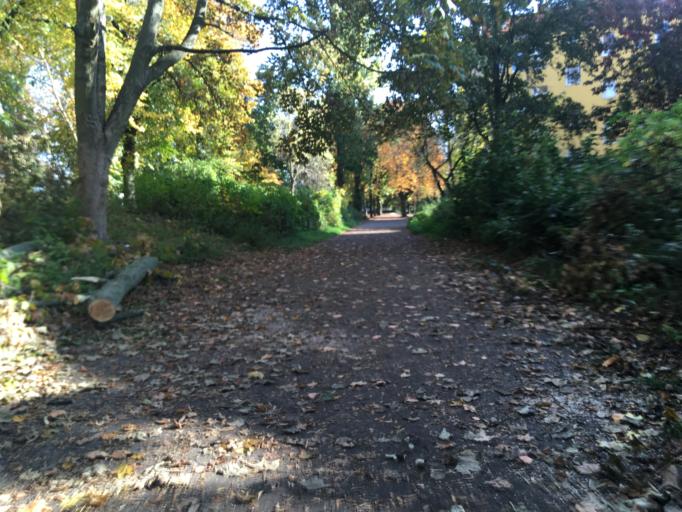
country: DE
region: Berlin
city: Wedding Bezirk
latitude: 52.5635
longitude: 13.3577
